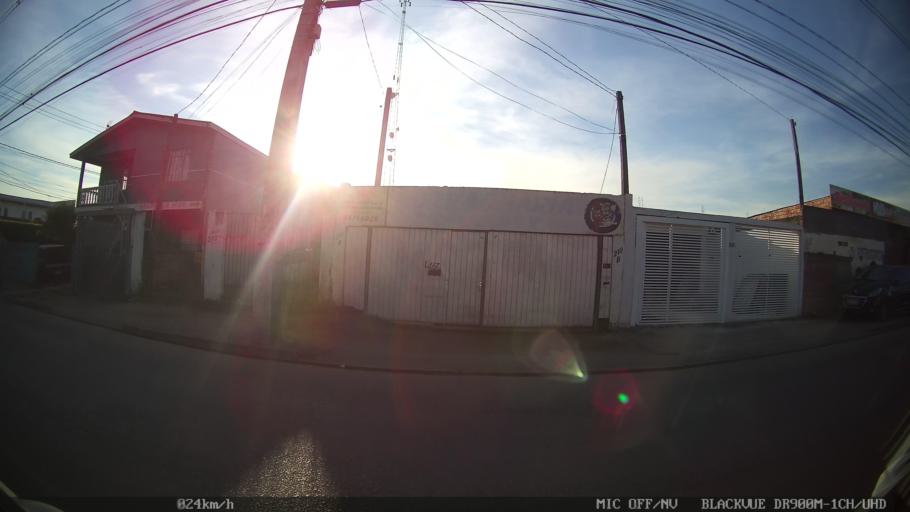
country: BR
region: Parana
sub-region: Pinhais
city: Pinhais
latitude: -25.4538
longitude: -49.1512
